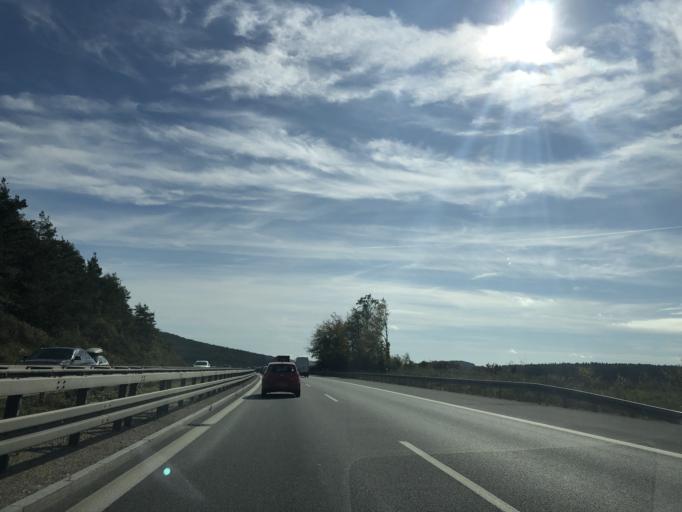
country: DE
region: Bavaria
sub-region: Upper Palatinate
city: Velburg
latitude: 49.2139
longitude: 11.6497
